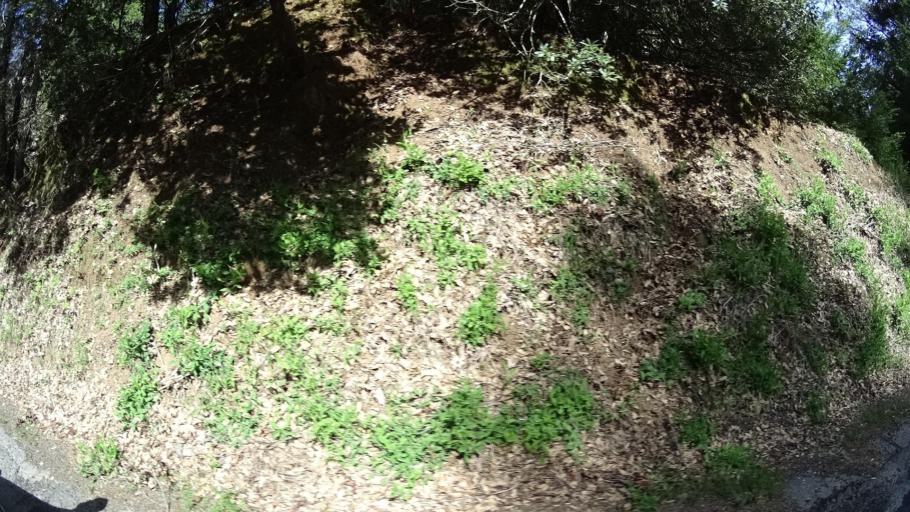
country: US
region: California
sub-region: Humboldt County
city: Redway
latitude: 40.3967
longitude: -123.7456
